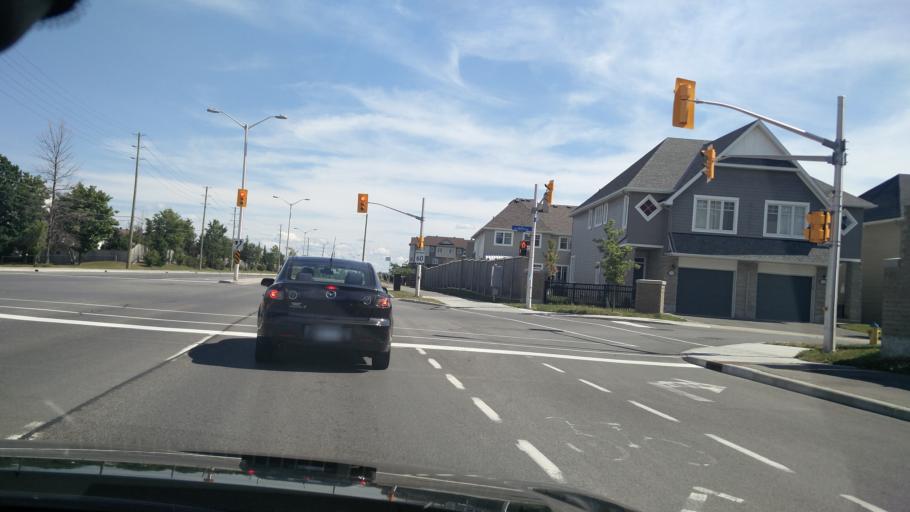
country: CA
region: Ontario
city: Bells Corners
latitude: 45.2595
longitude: -75.7312
